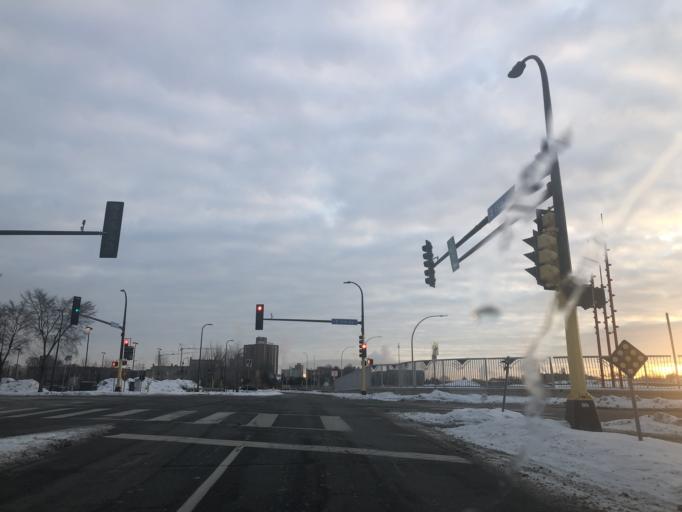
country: US
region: Minnesota
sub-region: Hennepin County
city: Minneapolis
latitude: 44.9674
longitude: -93.2778
